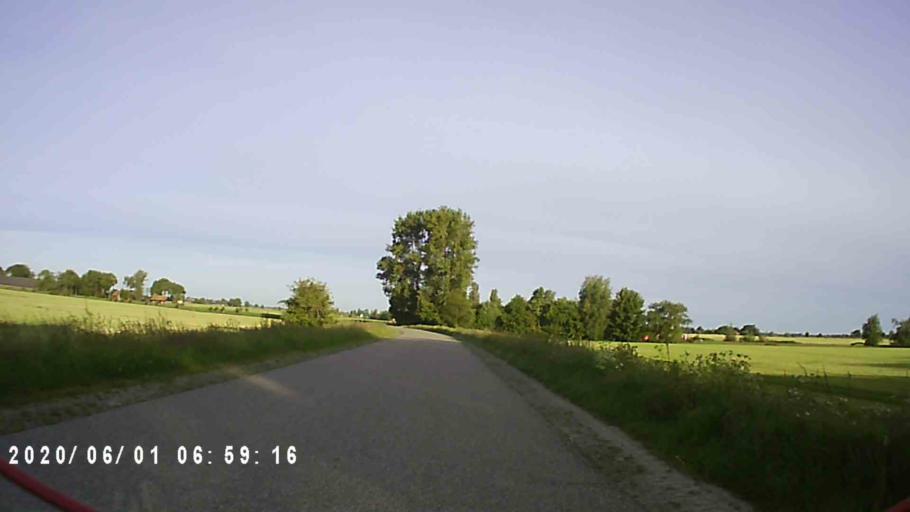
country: NL
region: Friesland
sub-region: Gemeente Kollumerland en Nieuwkruisland
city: Kollumerzwaag
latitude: 53.3203
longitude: 6.0961
